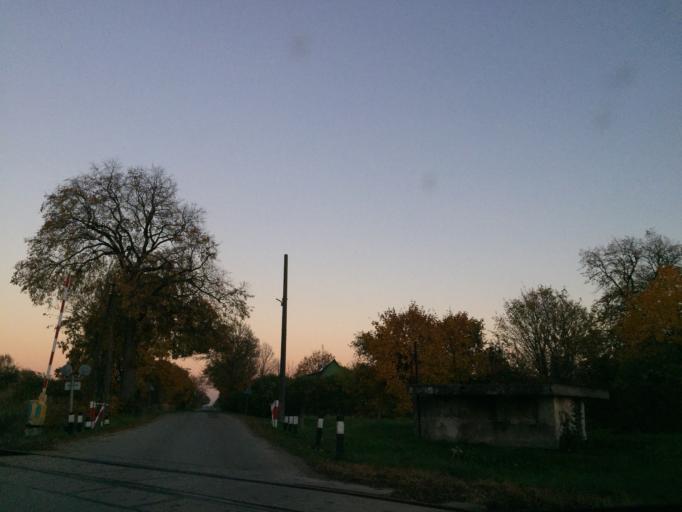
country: LT
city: Akmene
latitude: 56.3811
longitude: 22.6335
